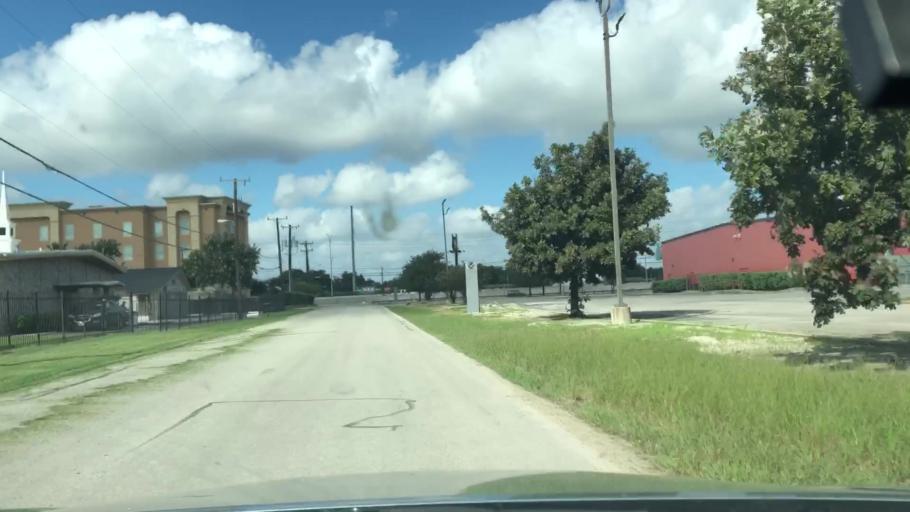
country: US
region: Texas
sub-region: Bexar County
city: Windcrest
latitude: 29.4921
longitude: -98.3993
